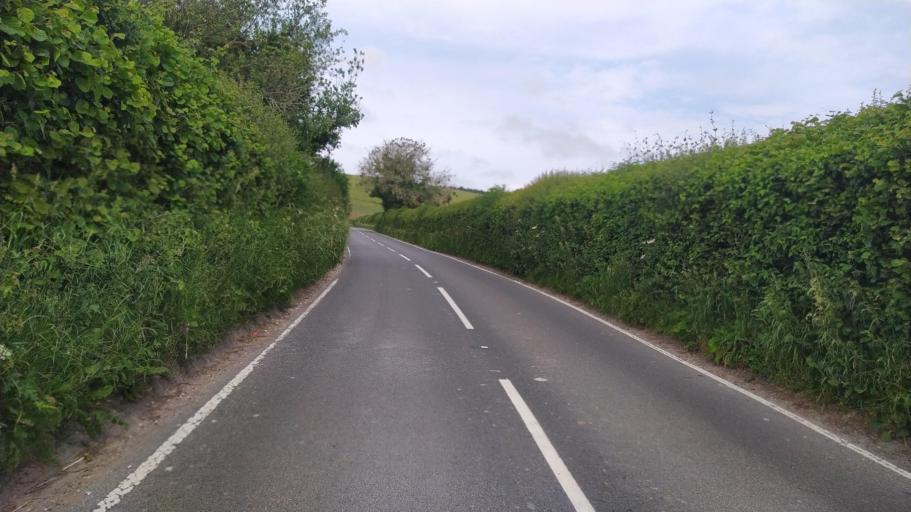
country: GB
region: England
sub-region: Dorset
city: Dorchester
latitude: 50.7903
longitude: -2.4753
